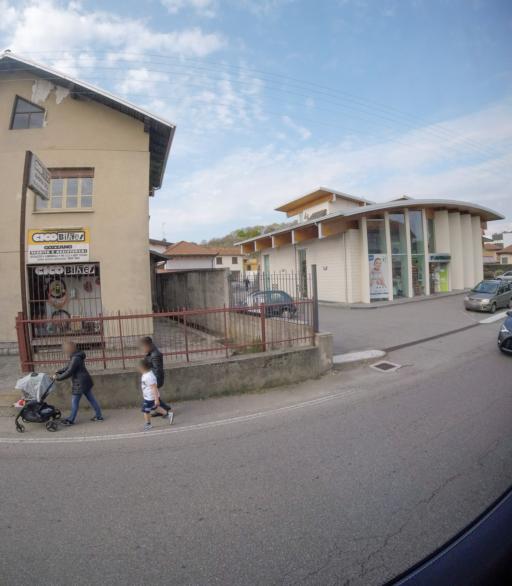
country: IT
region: Piedmont
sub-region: Provincia di Novara
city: Gozzano
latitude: 45.7429
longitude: 8.4349
